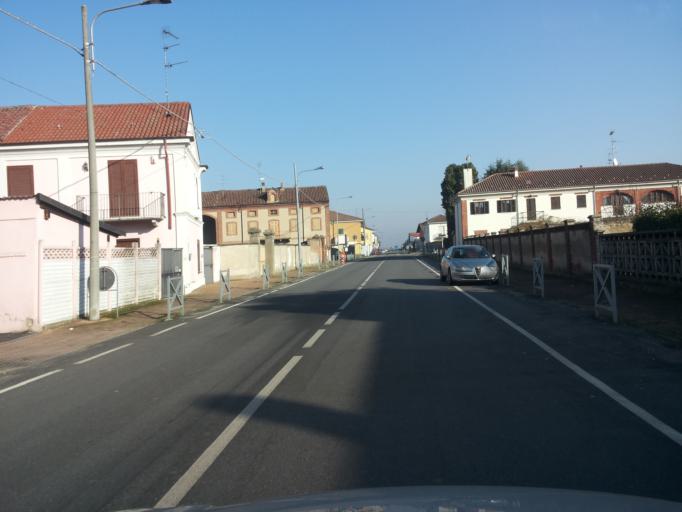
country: IT
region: Piedmont
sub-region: Provincia di Vercelli
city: Desana
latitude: 45.2713
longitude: 8.3604
